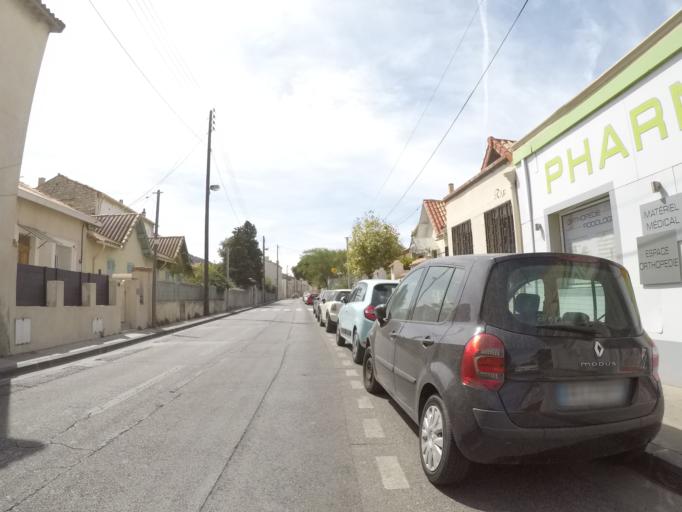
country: FR
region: Provence-Alpes-Cote d'Azur
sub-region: Departement des Bouches-du-Rhone
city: Marseille 08
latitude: 43.2385
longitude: 5.3650
